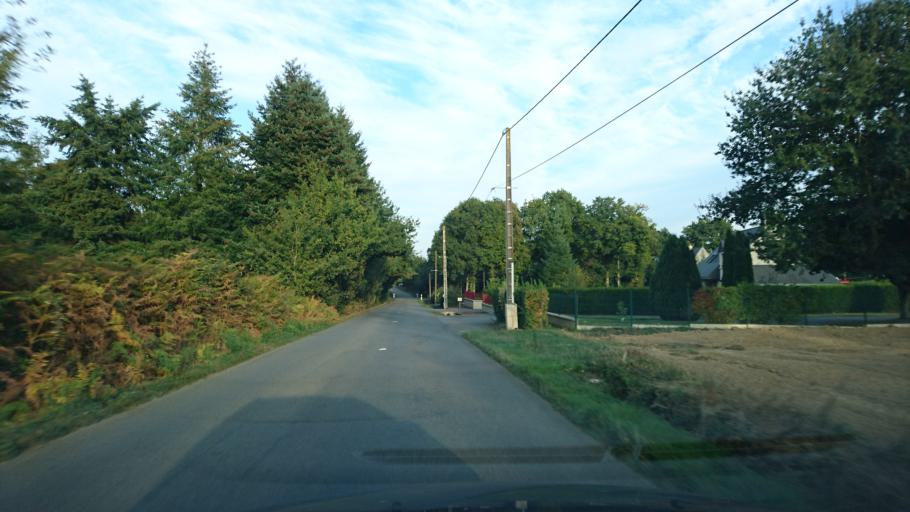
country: FR
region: Brittany
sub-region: Departement d'Ille-et-Vilaine
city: Sainte-Marie
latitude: 47.6794
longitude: -2.0258
